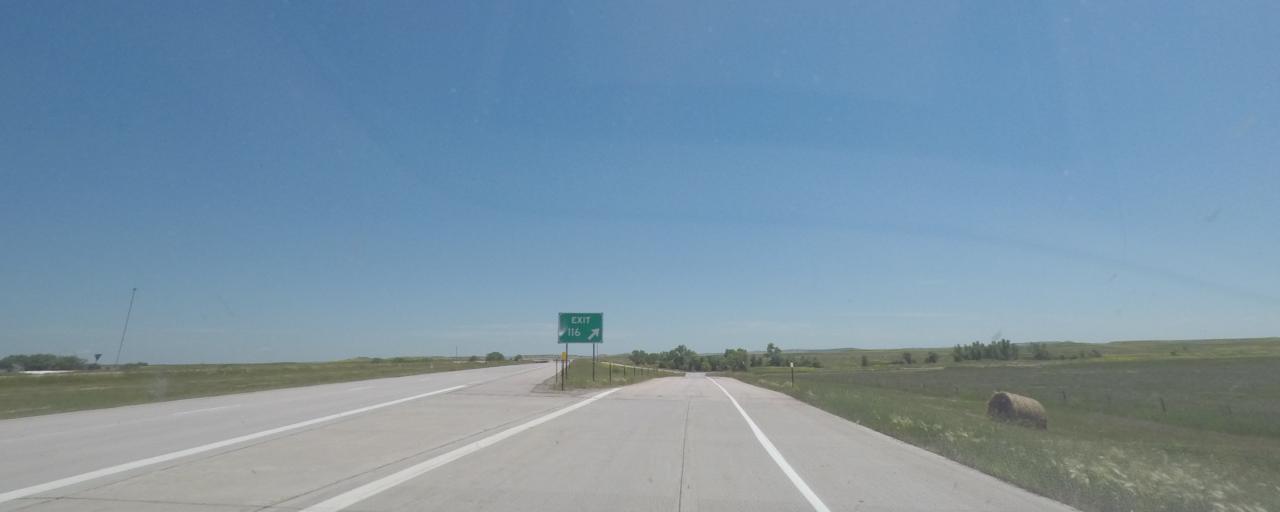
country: US
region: South Dakota
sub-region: Haakon County
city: Philip
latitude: 43.9392
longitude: -102.1549
